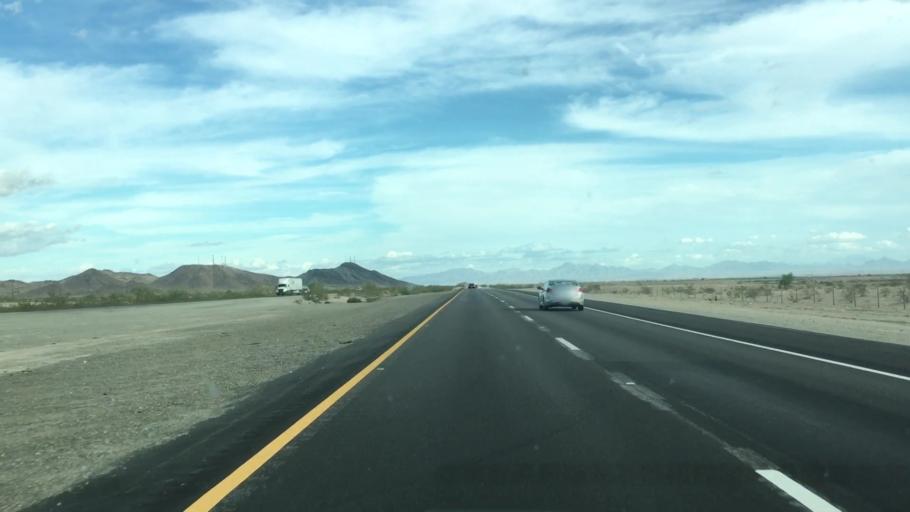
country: US
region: California
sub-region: Riverside County
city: Mesa Verde
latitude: 33.6097
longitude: -114.8066
